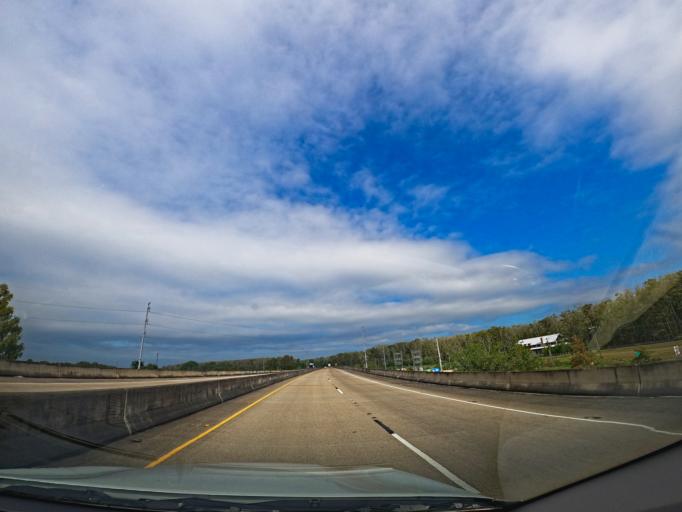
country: US
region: Louisiana
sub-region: Saint Mary Parish
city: Morgan City
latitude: 29.6979
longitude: -91.1819
